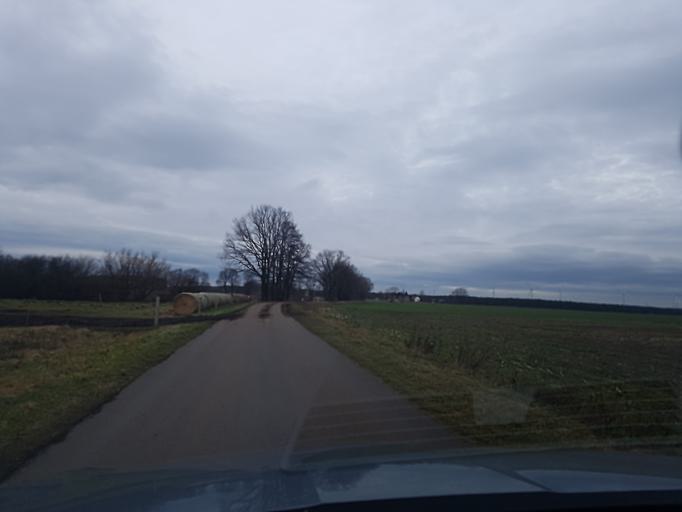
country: DE
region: Brandenburg
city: Schilda
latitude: 51.6236
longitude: 13.3532
